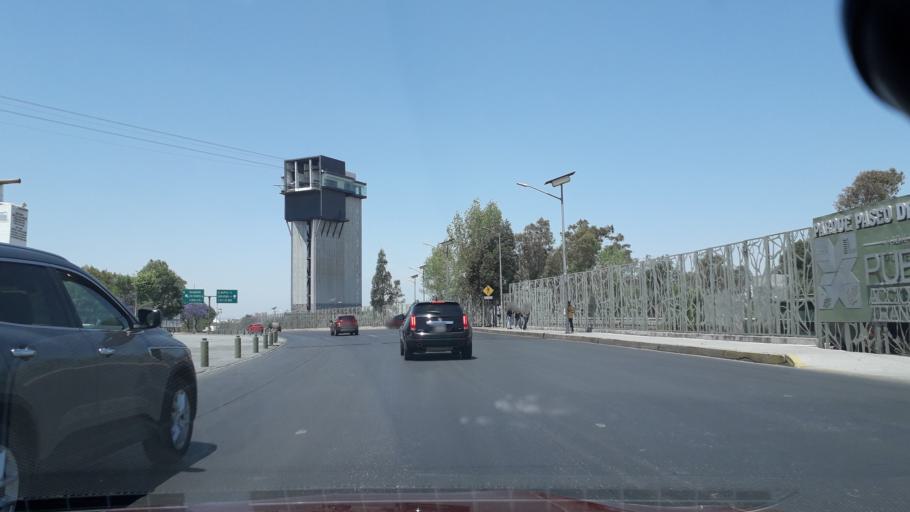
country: MX
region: Puebla
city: Puebla
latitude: 19.0609
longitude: -98.1843
